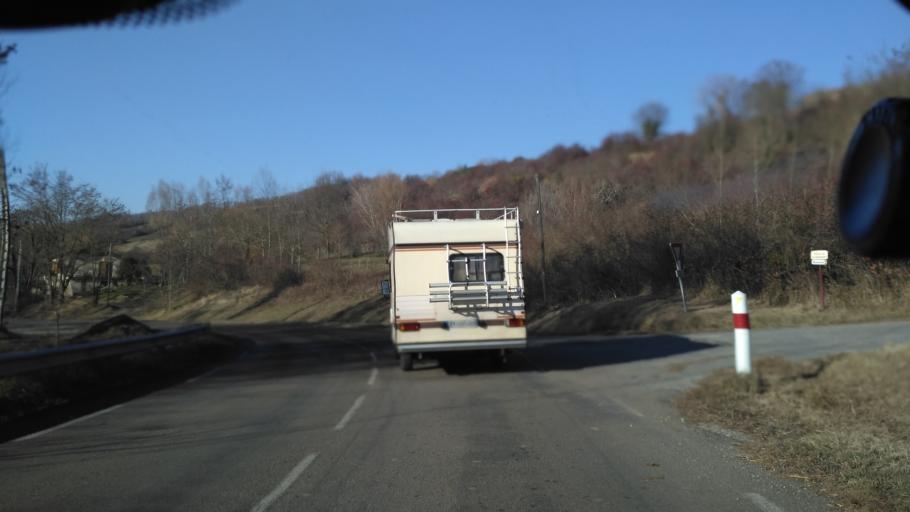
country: FR
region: Rhone-Alpes
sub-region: Departement de l'Isere
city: Saint-Antoine-l'Abbaye
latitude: 45.1540
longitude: 5.1412
